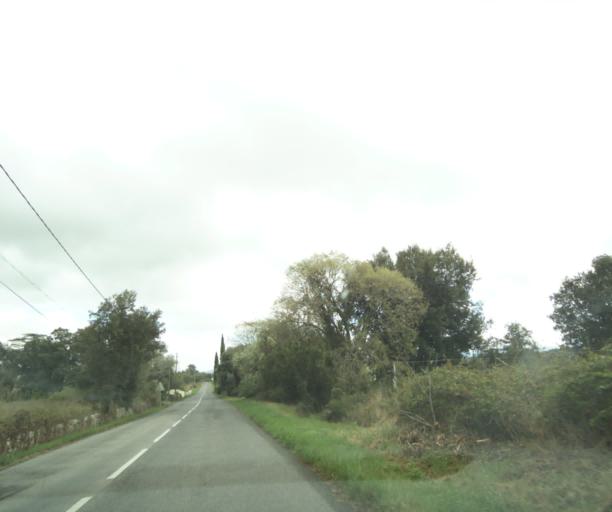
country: FR
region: Languedoc-Roussillon
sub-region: Departement de l'Herault
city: Murviel-les-Montpellier
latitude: 43.5956
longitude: 3.7471
